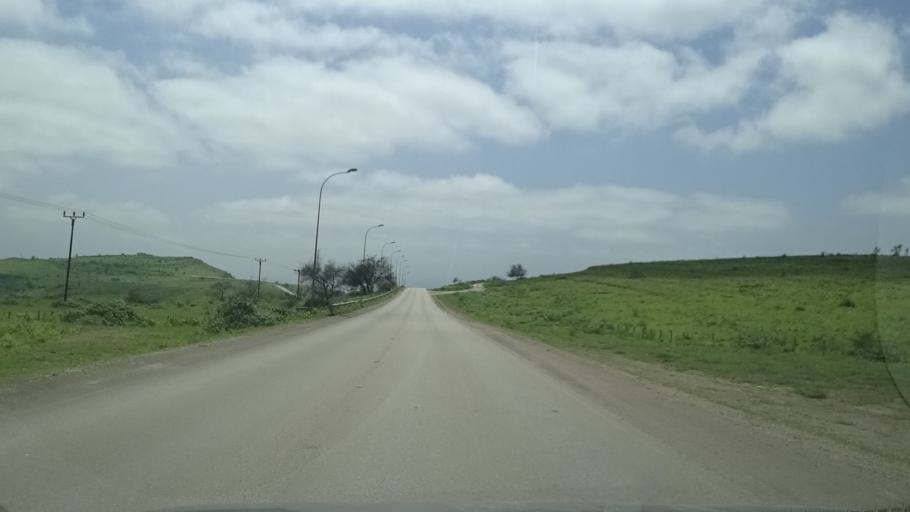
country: OM
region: Zufar
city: Salalah
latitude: 17.1713
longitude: 54.2300
